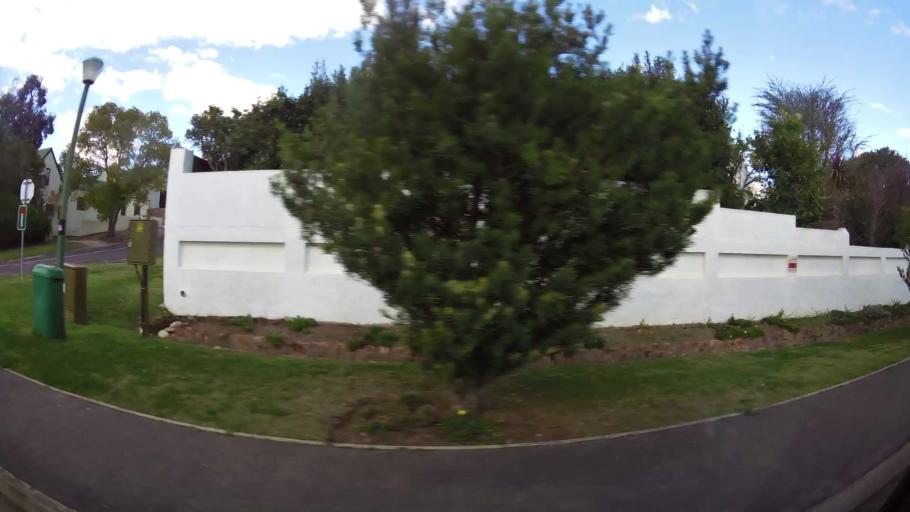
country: ZA
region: Western Cape
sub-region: Overberg District Municipality
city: Swellendam
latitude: -34.0144
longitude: 20.4555
